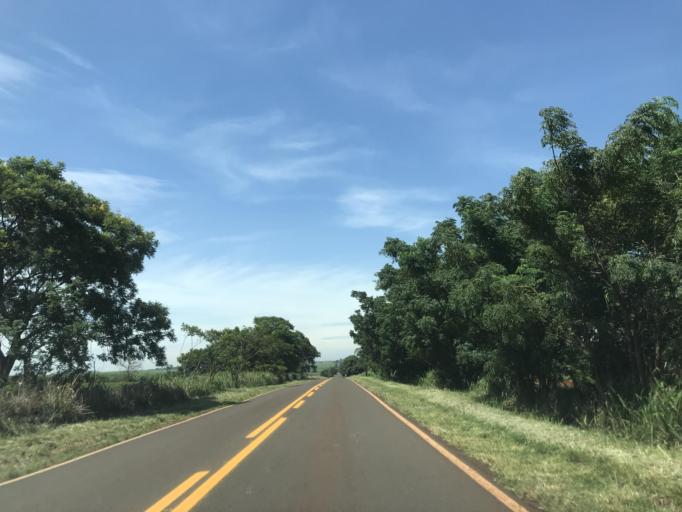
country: BR
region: Parana
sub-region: Terra Rica
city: Terra Rica
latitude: -22.8012
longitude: -52.6534
